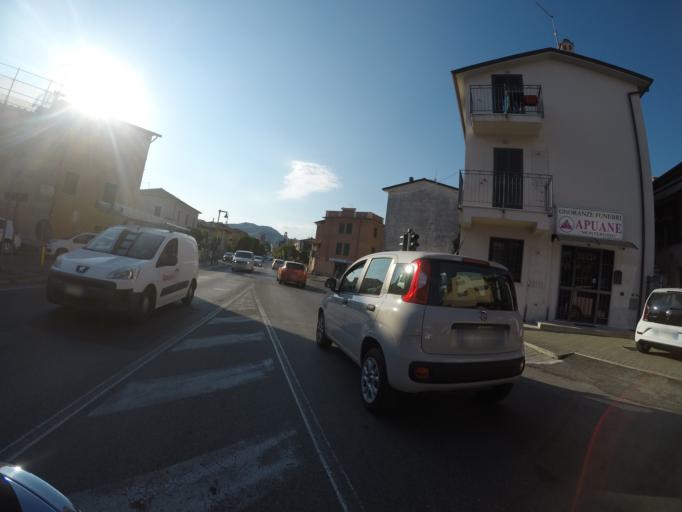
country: IT
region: Tuscany
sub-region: Provincia di Massa-Carrara
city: Massa
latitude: 44.0315
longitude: 10.1440
